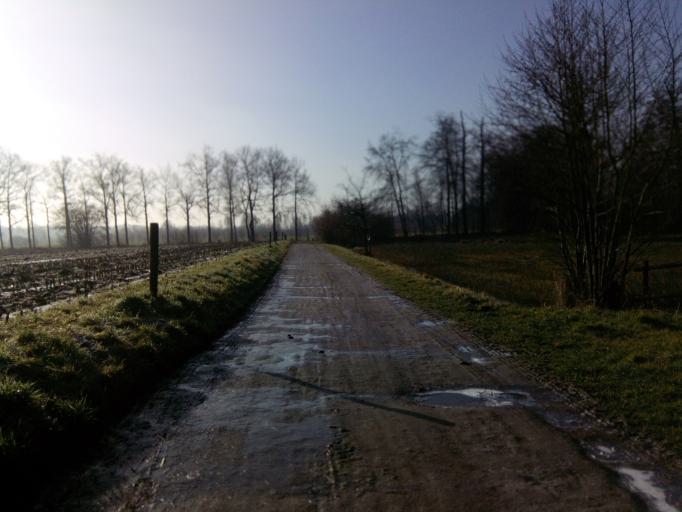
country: NL
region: Utrecht
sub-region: Gemeente Woudenberg
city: Woudenberg
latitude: 52.1055
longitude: 5.3952
